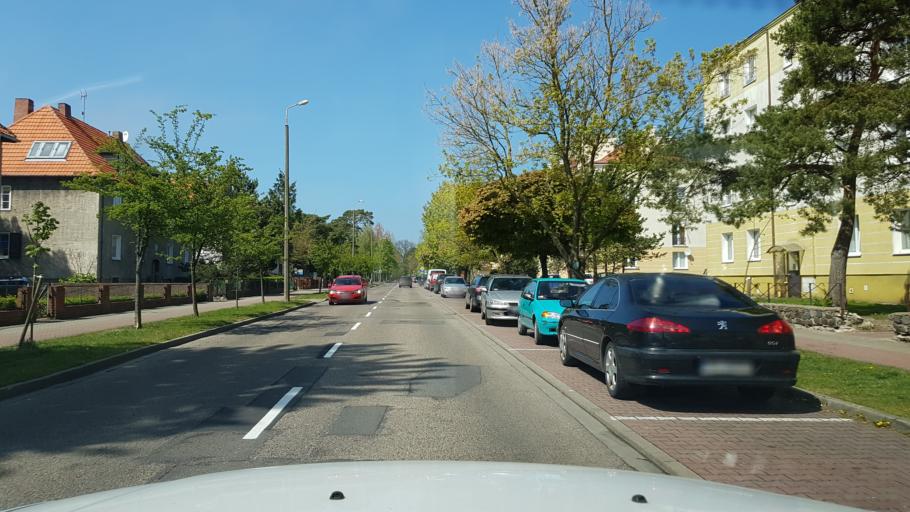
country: PL
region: Pomeranian Voivodeship
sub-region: Powiat slupski
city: Ustka
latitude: 54.5845
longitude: 16.8655
